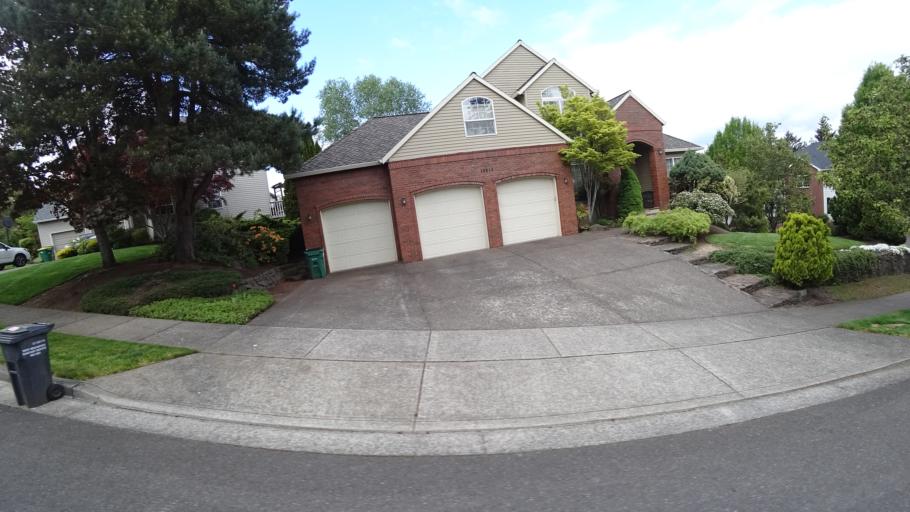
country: US
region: Oregon
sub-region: Washington County
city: Beaverton
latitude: 45.4482
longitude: -122.8396
